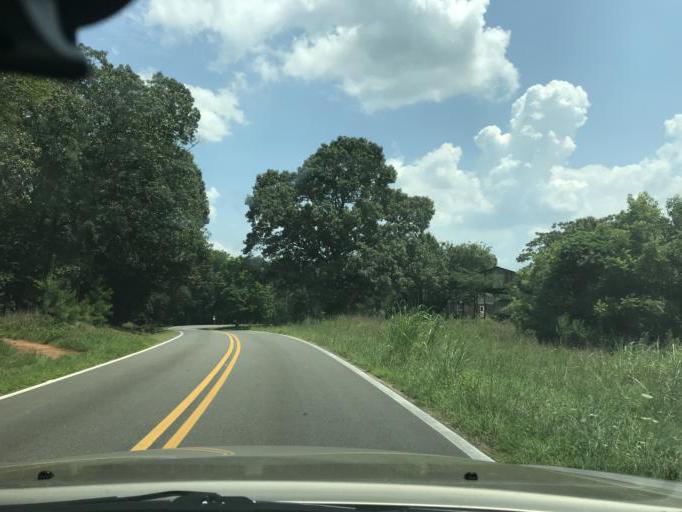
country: US
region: Georgia
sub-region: Forsyth County
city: Cumming
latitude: 34.2628
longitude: -84.2224
